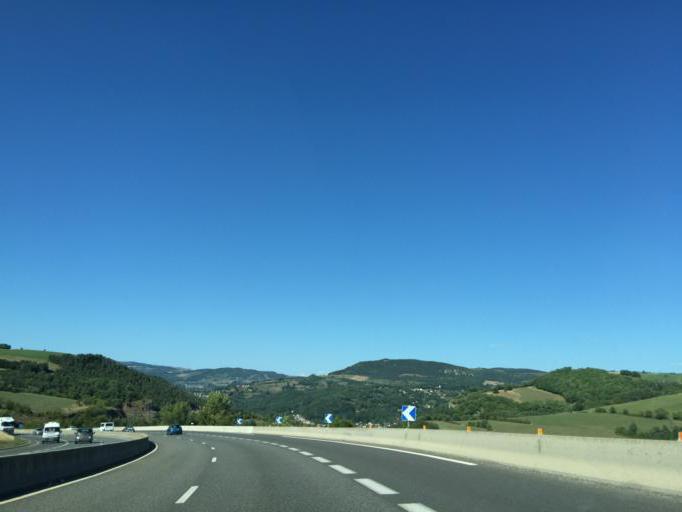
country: FR
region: Languedoc-Roussillon
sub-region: Departement de la Lozere
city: La Canourgue
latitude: 44.4191
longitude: 3.1842
